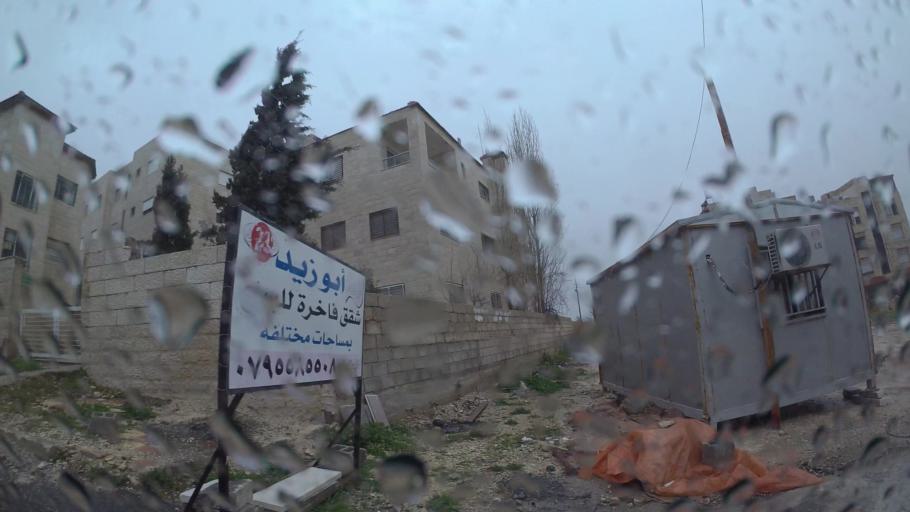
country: JO
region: Amman
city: Al Jubayhah
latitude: 32.0432
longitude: 35.8937
